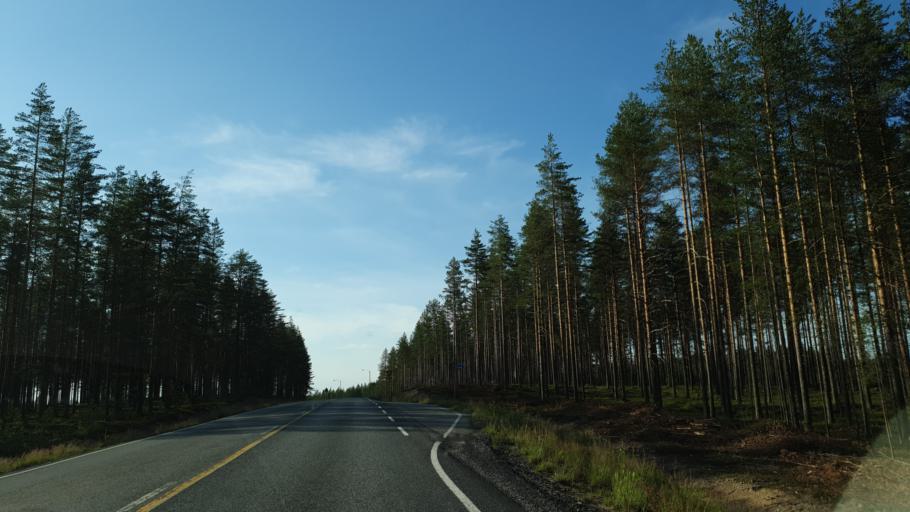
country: FI
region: Kainuu
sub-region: Kehys-Kainuu
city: Kuhmo
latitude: 64.0967
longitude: 29.4766
